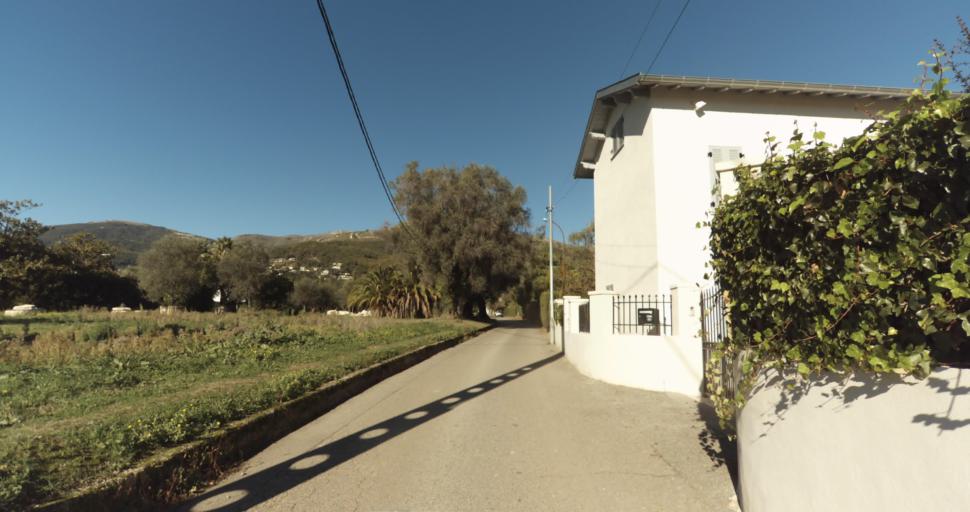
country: FR
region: Provence-Alpes-Cote d'Azur
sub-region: Departement des Alpes-Maritimes
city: Vence
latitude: 43.7207
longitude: 7.0900
